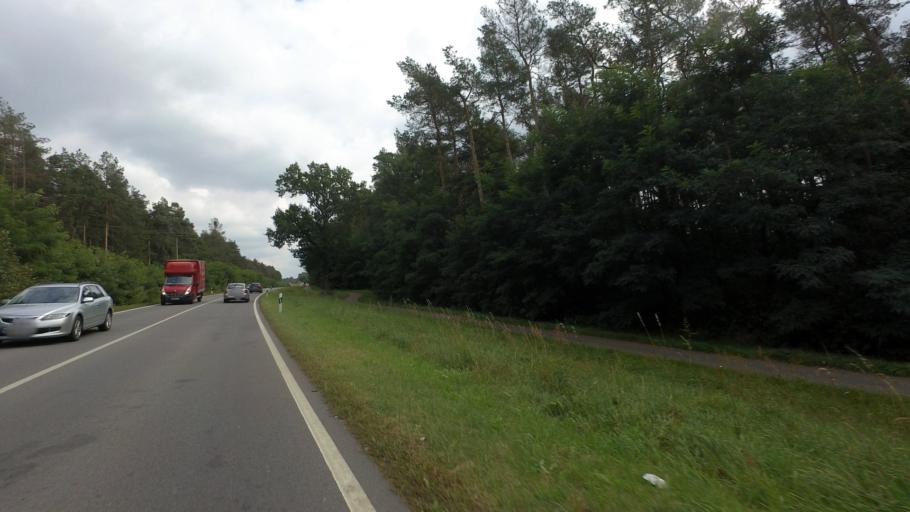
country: DE
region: Brandenburg
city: Finsterwalde
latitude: 51.6365
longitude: 13.7474
